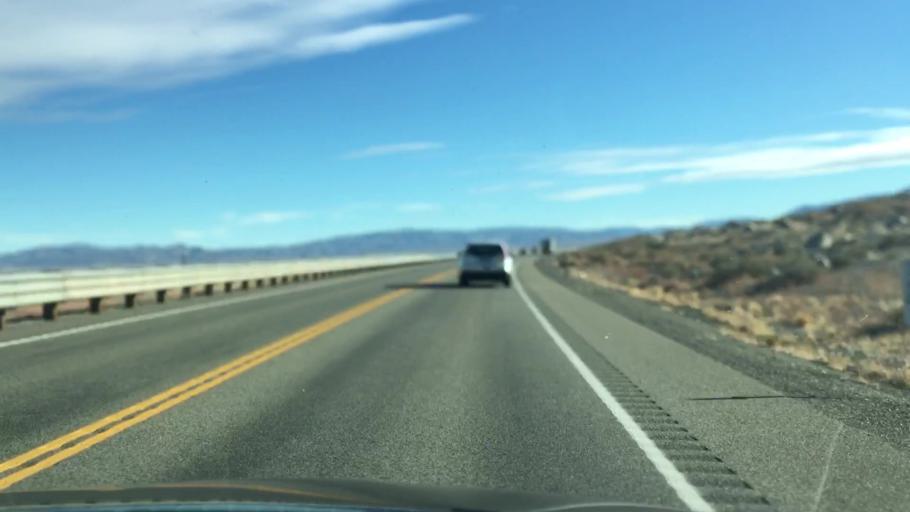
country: US
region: Nevada
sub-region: Mineral County
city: Hawthorne
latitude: 38.6090
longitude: -118.7149
